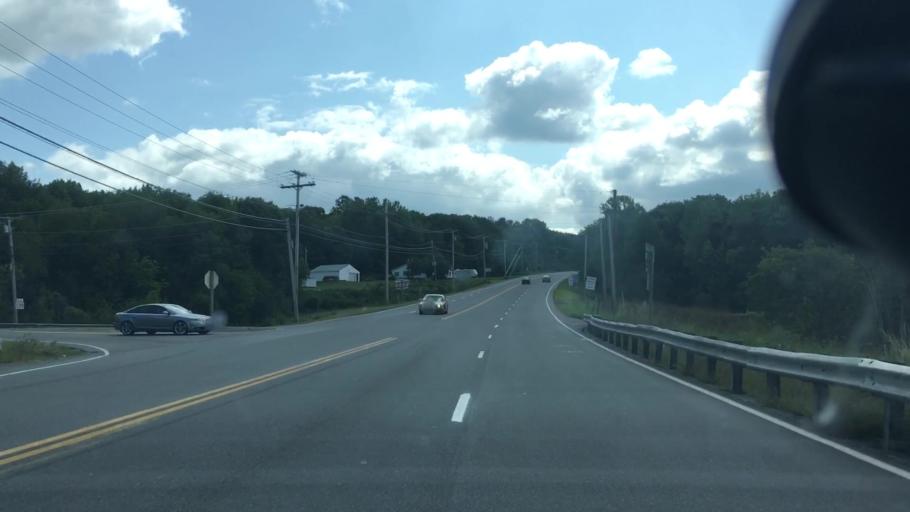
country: US
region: Maine
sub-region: Kennebec County
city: Waterville
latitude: 44.5988
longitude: -69.6556
